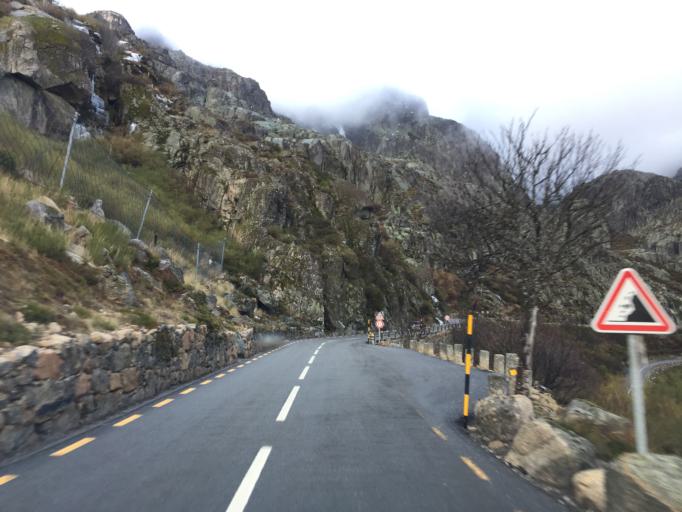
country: PT
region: Castelo Branco
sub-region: Covilha
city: Covilha
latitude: 40.3253
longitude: -7.5839
